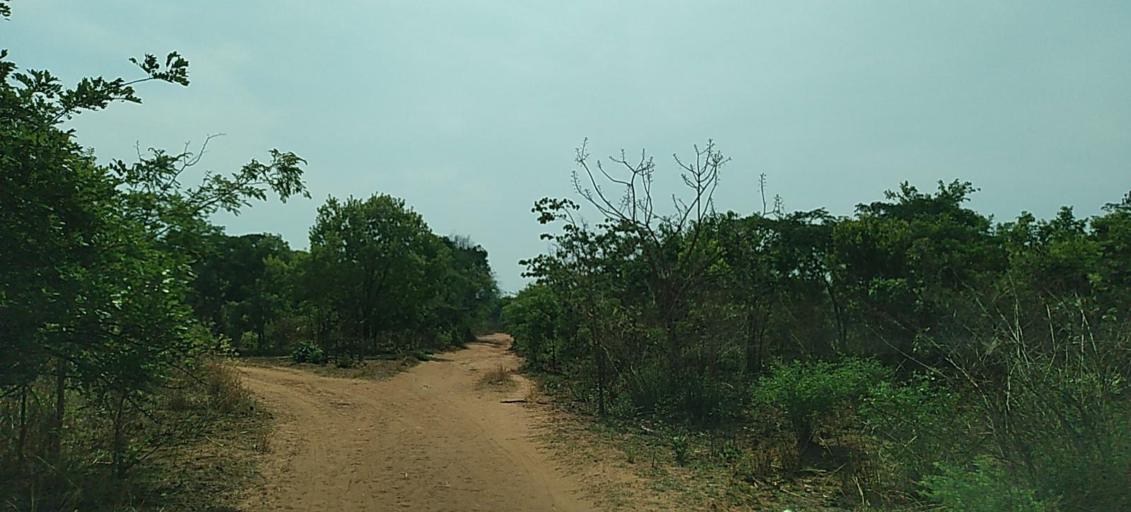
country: ZM
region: Copperbelt
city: Ndola
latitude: -13.2103
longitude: 28.7455
